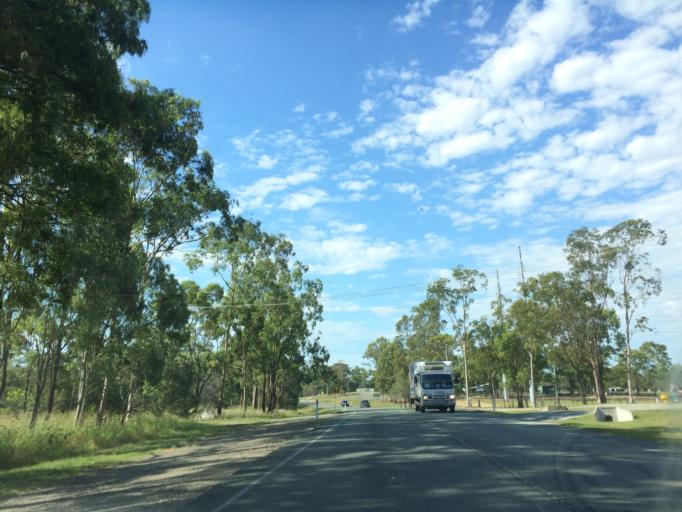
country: AU
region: Queensland
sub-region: Logan
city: Park Ridge South
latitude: -27.7275
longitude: 152.9843
